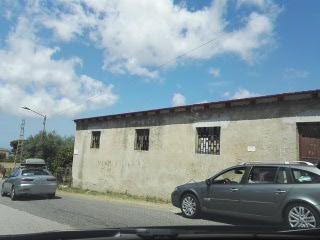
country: IT
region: Calabria
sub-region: Provincia di Vibo-Valentia
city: Spilinga
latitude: 38.6234
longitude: 15.8904
